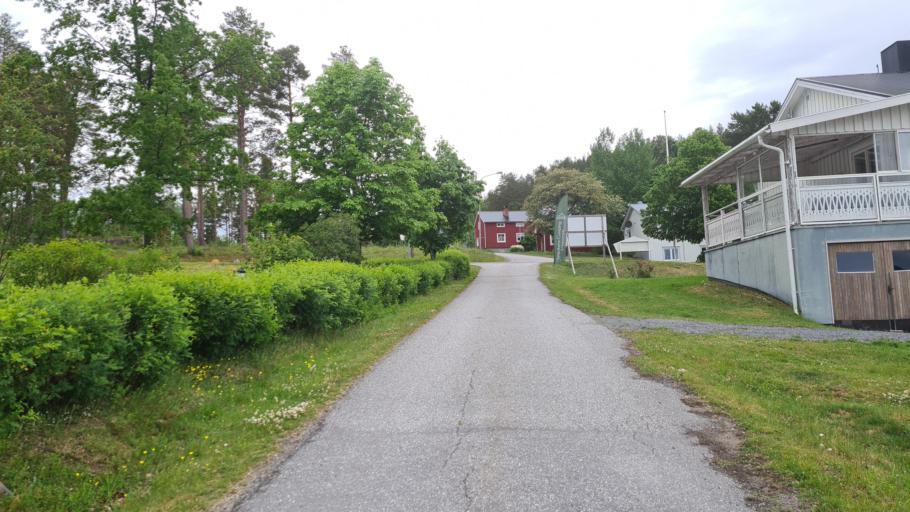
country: SE
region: Vaesternorrland
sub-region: Kramfors Kommun
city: Nordingra
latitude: 62.9720
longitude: 18.4248
